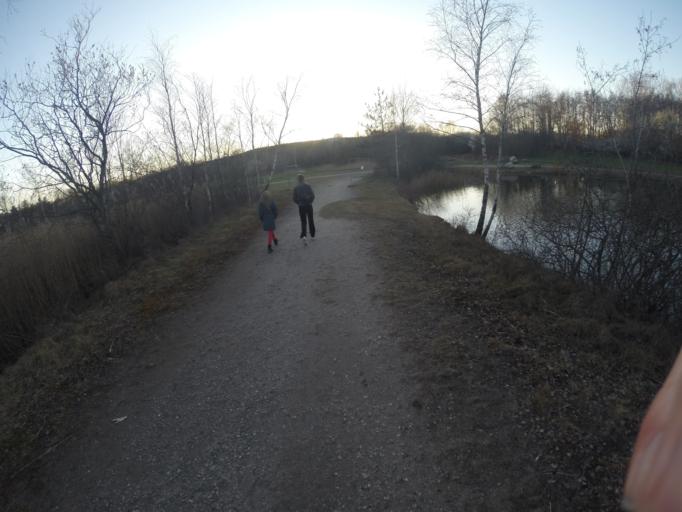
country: DK
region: Capital Region
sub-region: Hoje-Taastrup Kommune
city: Flong
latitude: 55.6416
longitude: 12.1840
